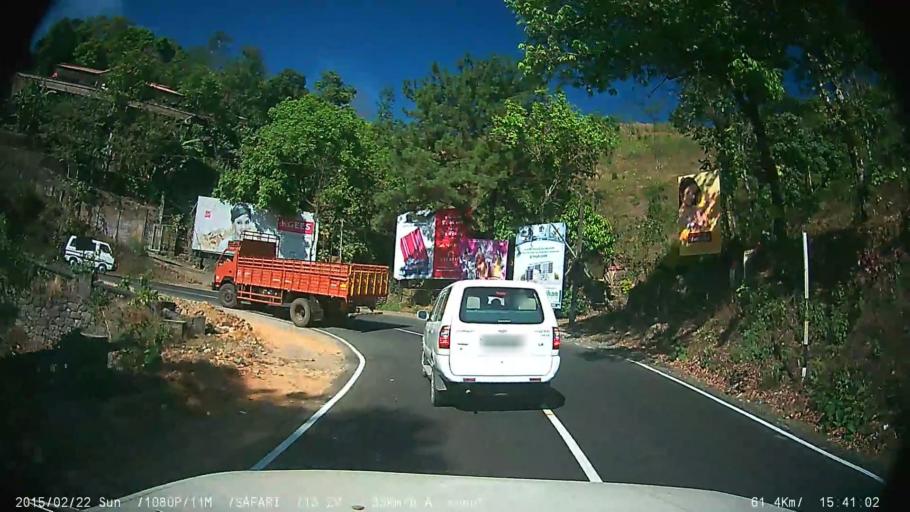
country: IN
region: Kerala
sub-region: Kottayam
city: Erattupetta
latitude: 9.5732
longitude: 76.9756
